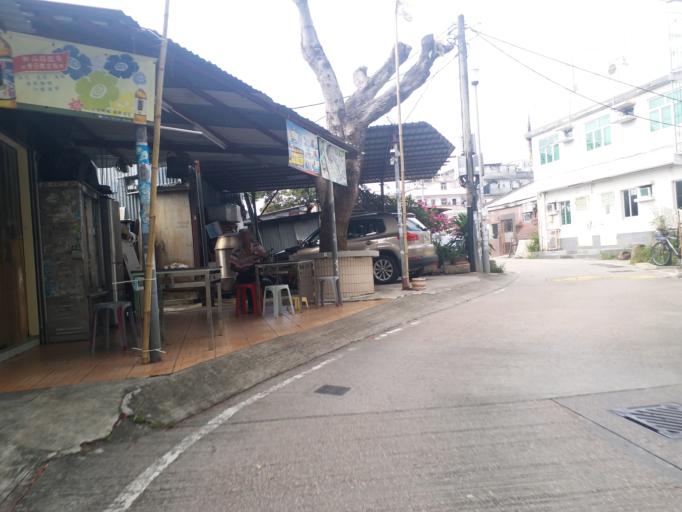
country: HK
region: Yuen Long
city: Yuen Long Kau Hui
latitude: 22.4446
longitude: 114.0073
